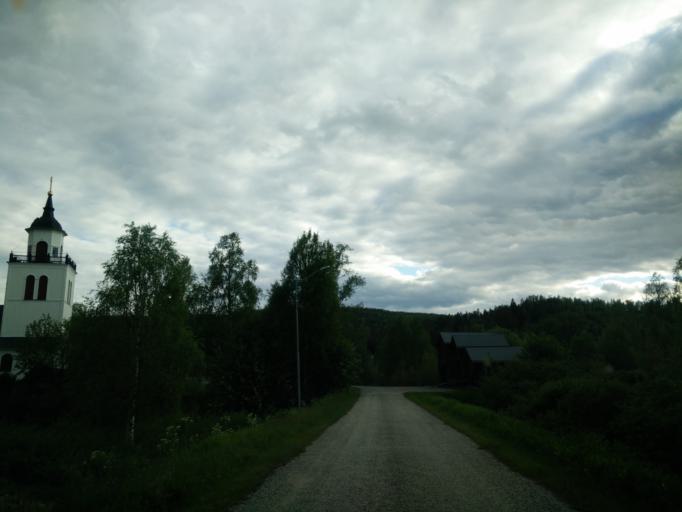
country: SE
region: Jaemtland
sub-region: Harjedalens Kommun
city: Sveg
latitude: 62.2777
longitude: 14.8051
